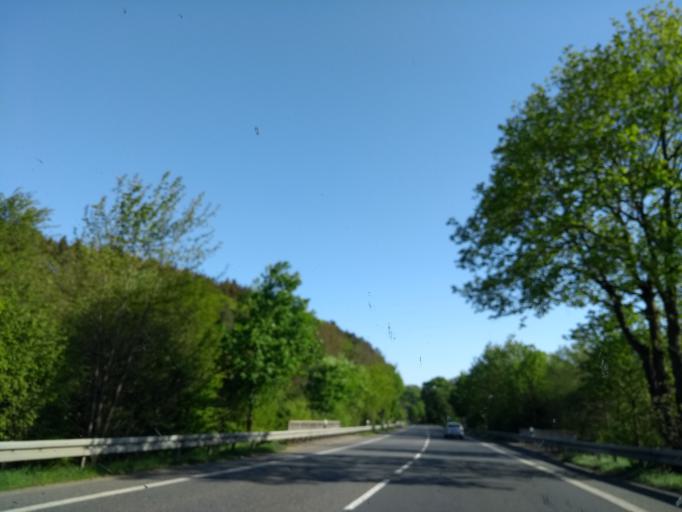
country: DE
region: Hesse
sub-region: Regierungsbezirk Giessen
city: Breidenbach
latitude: 50.8985
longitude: 8.4500
